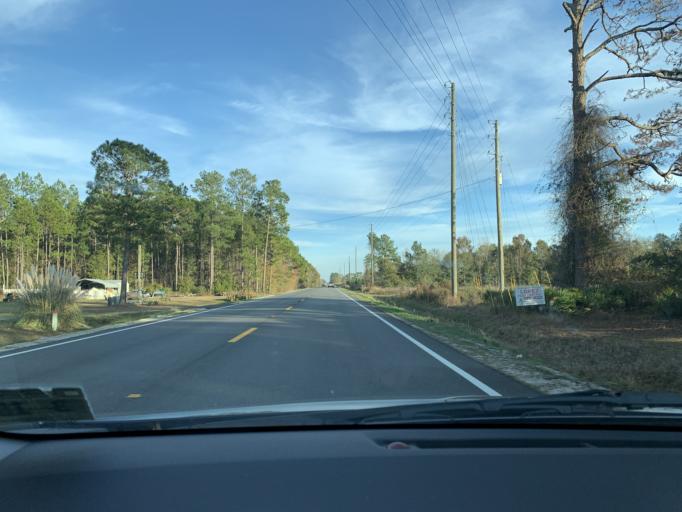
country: US
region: Georgia
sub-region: Irwin County
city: Ocilla
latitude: 31.5891
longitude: -83.0896
